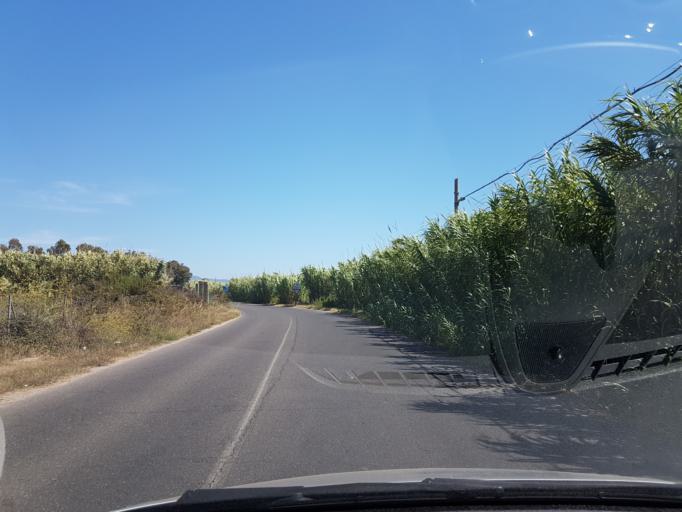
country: IT
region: Sardinia
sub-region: Provincia di Oristano
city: Cabras
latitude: 39.9215
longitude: 8.5356
